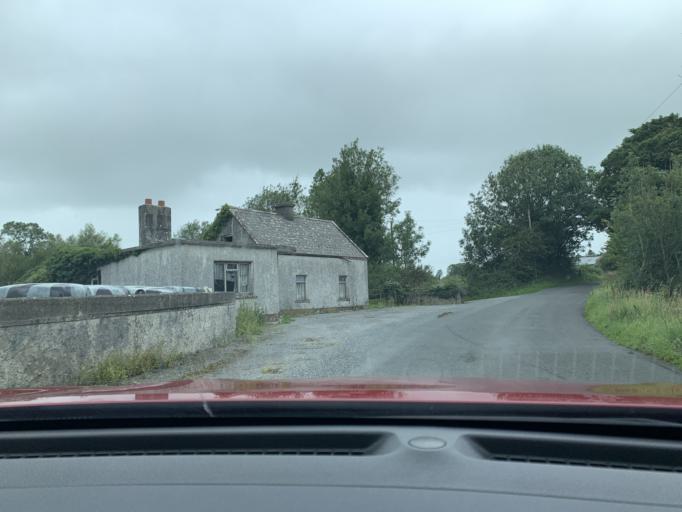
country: IE
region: Connaught
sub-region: County Leitrim
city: Carrick-on-Shannon
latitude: 53.8590
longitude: -8.1453
